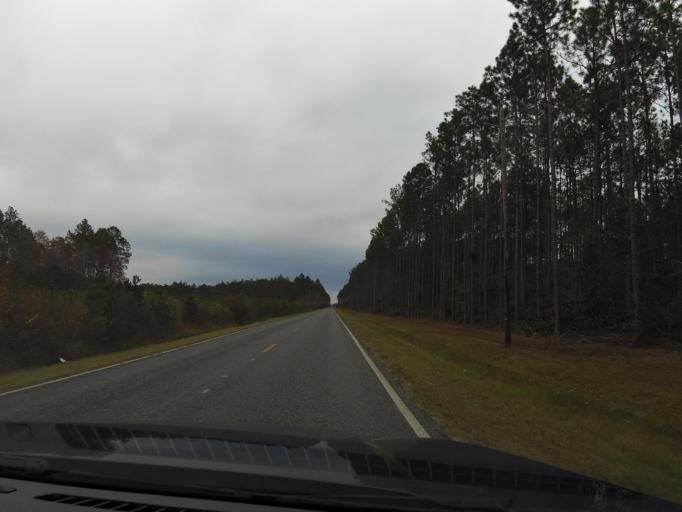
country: US
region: Georgia
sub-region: Charlton County
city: Folkston
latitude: 30.8919
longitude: -82.0639
